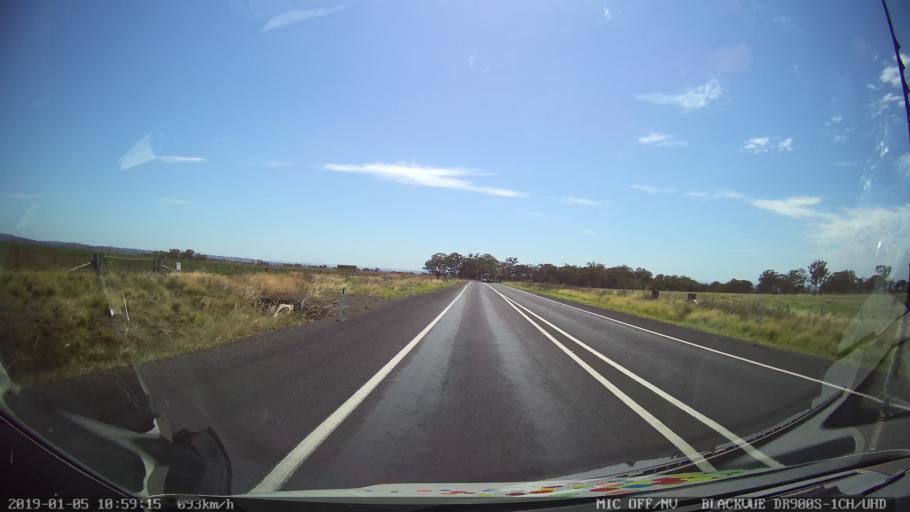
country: AU
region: New South Wales
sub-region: Warrumbungle Shire
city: Coonabarabran
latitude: -31.4158
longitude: 149.1929
